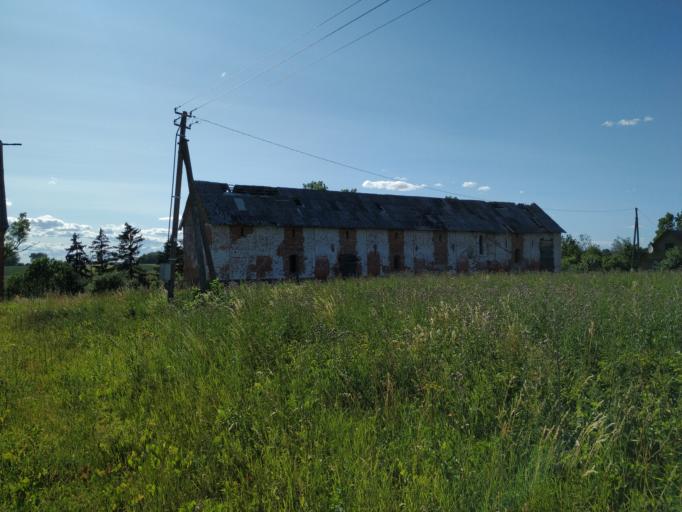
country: LT
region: Panevezys
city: Pasvalys
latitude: 56.1487
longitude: 24.4563
